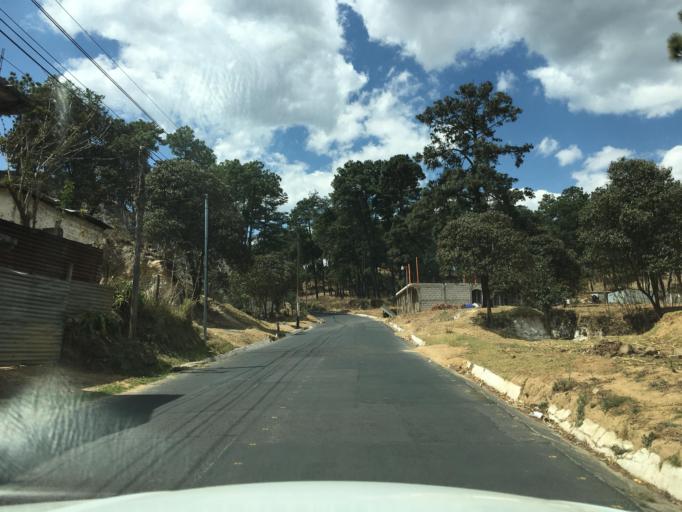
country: GT
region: Totonicapan
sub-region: Municipio de San Andres Xecul
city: San Andres Xecul
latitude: 14.9053
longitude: -91.4609
